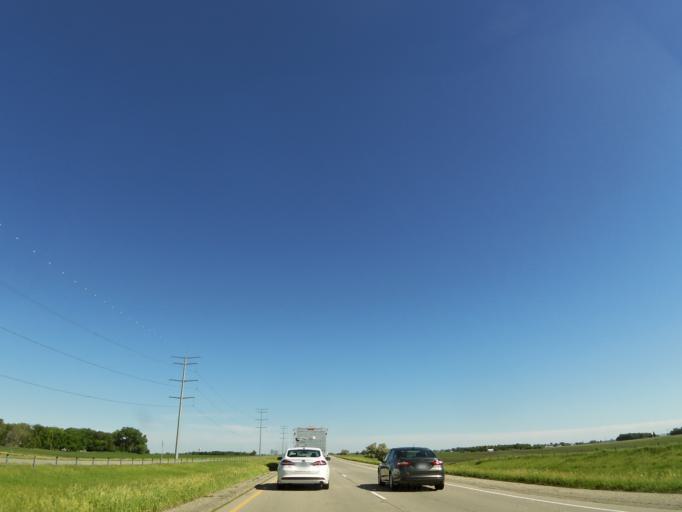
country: US
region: Minnesota
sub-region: Clay County
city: Barnesville
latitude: 46.5714
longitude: -96.3255
